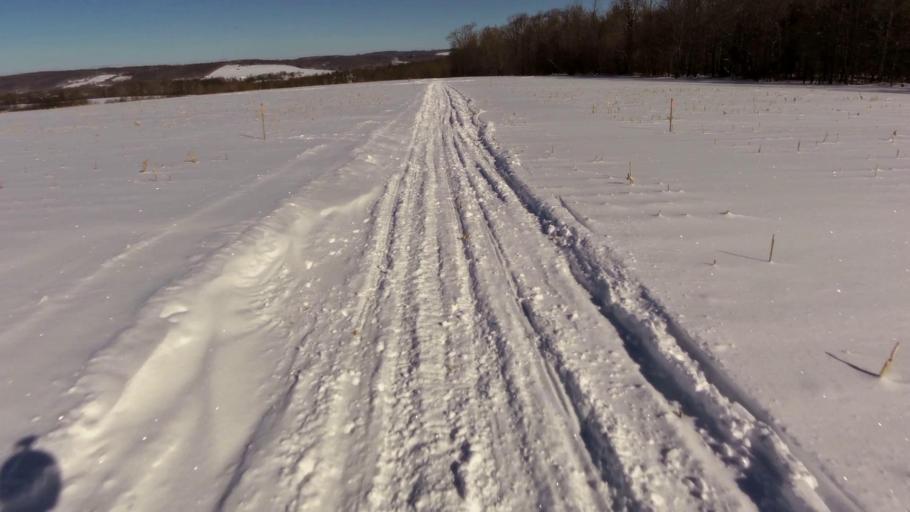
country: US
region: New York
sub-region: Chautauqua County
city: Silver Creek
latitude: 42.3514
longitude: -79.1262
